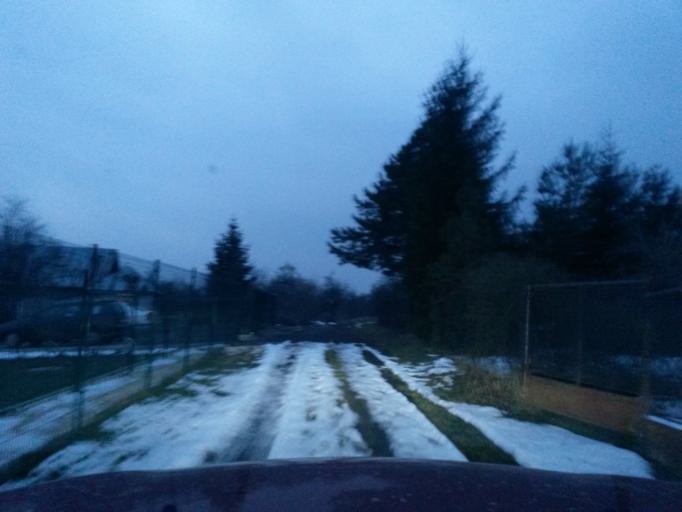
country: SK
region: Kosicky
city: Secovce
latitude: 48.7122
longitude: 21.6295
